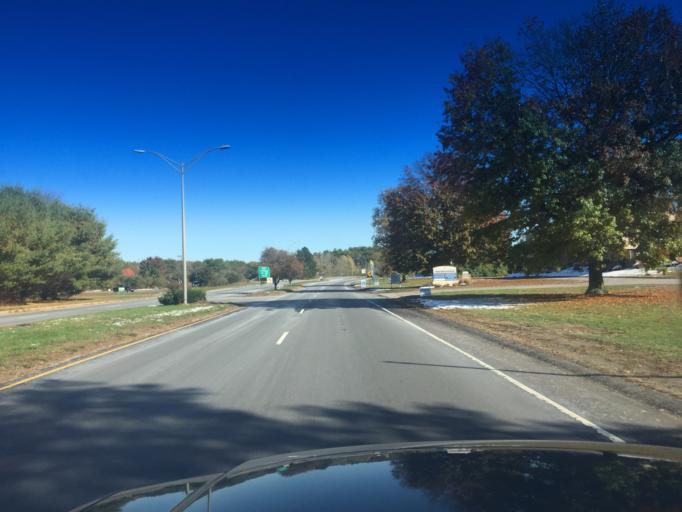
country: US
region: Massachusetts
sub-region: Bristol County
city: Raynham
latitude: 41.9603
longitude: -71.1277
